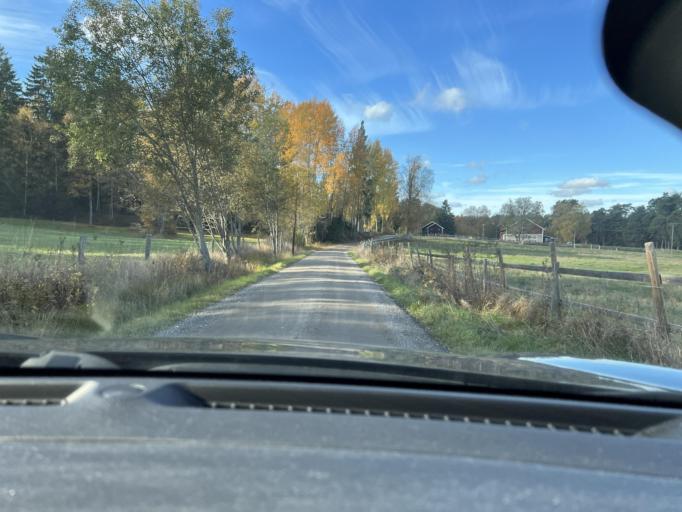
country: SE
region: Stockholm
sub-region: Vallentuna Kommun
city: Vallentuna
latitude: 59.5088
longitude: 18.1180
